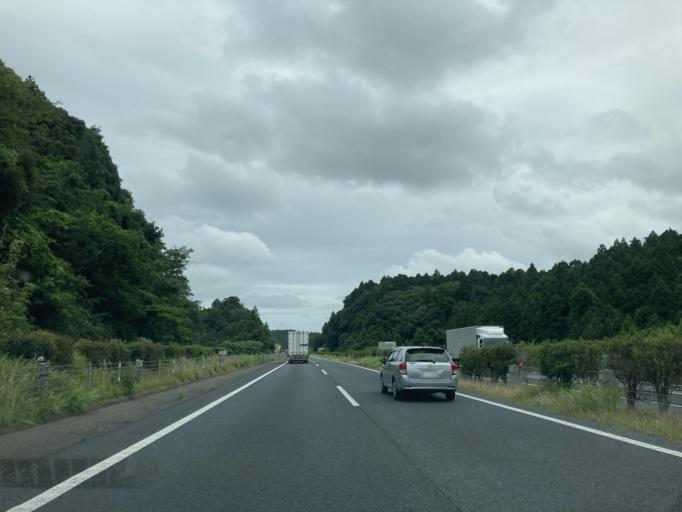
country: JP
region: Chiba
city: Sawara
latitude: 35.8588
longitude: 140.5238
